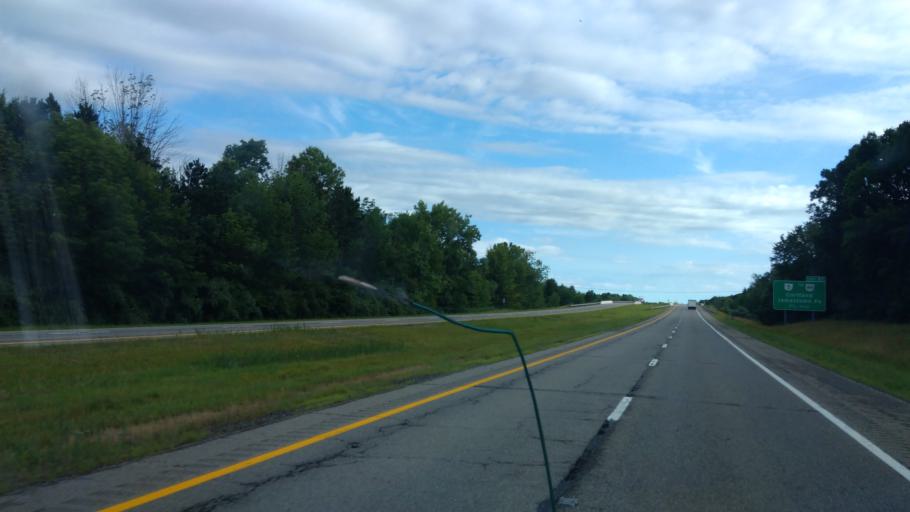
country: US
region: Ohio
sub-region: Trumbull County
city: Cortland
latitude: 41.3470
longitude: -80.7009
